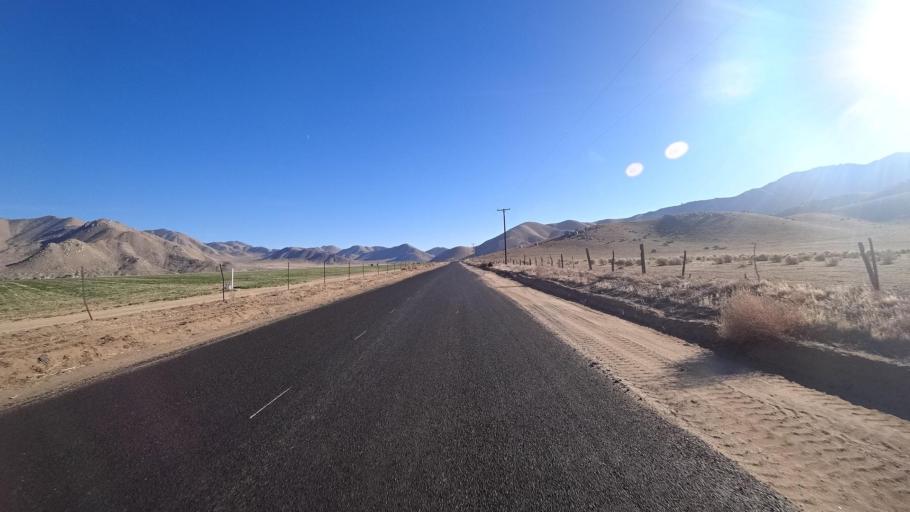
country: US
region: California
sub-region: Kern County
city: Weldon
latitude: 35.6351
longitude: -118.2643
